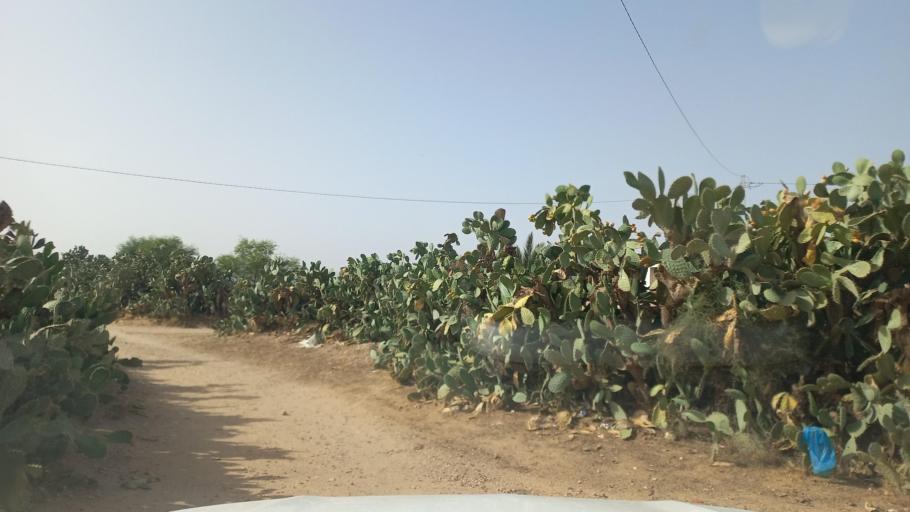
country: TN
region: Al Qasrayn
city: Kasserine
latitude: 35.2995
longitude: 8.9622
